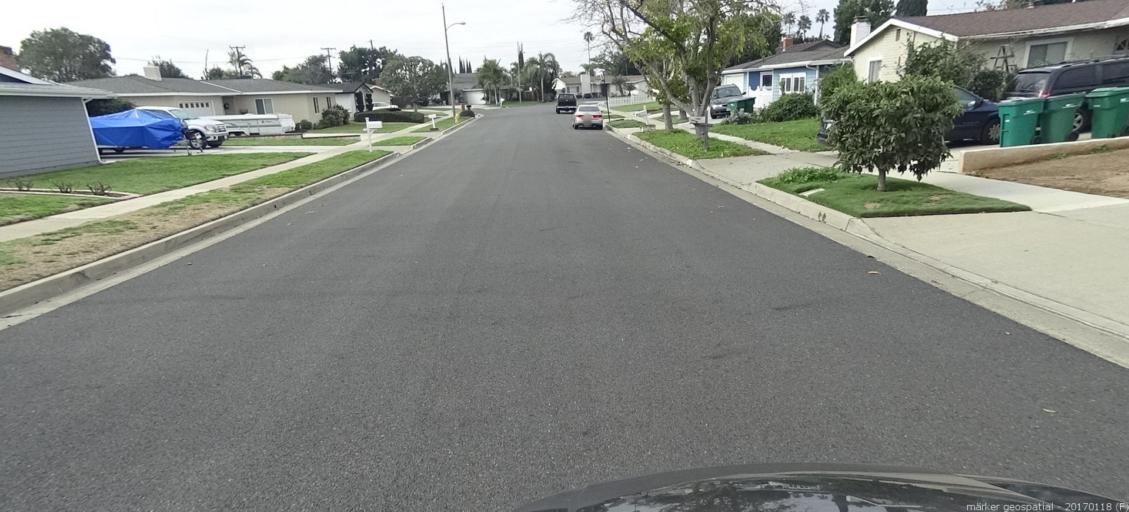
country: US
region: California
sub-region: Orange County
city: North Tustin
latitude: 33.7439
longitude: -117.8000
